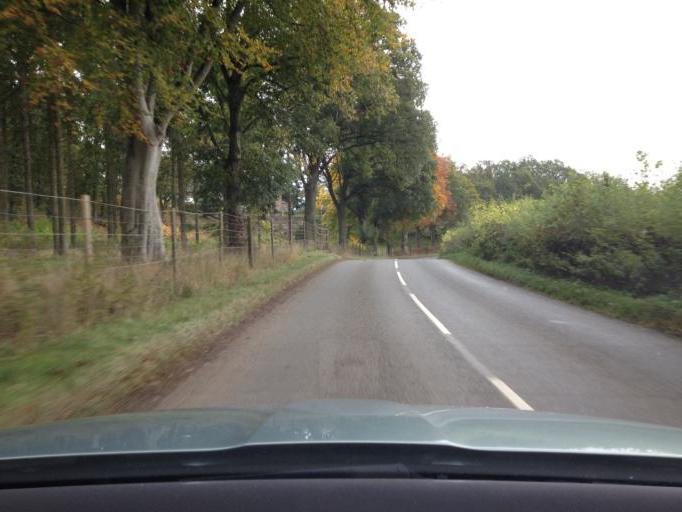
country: GB
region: Scotland
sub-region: Perth and Kinross
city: Stanley
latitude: 56.5190
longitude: -3.4007
